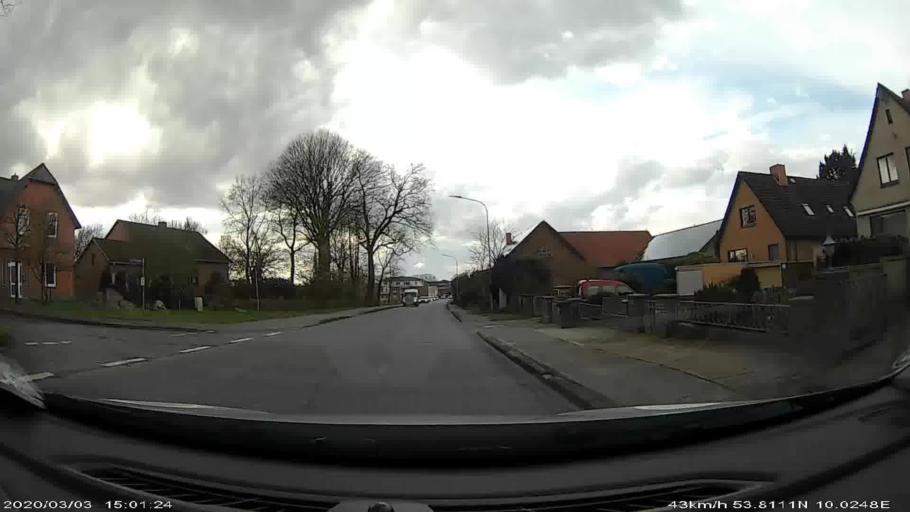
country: DE
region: Schleswig-Holstein
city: Kisdorf
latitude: 53.8113
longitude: 10.0252
